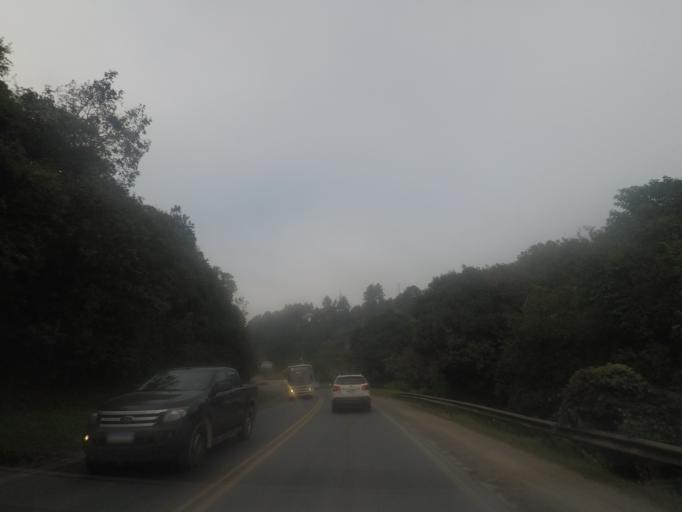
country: BR
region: Parana
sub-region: Almirante Tamandare
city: Almirante Tamandare
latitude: -25.3058
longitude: -49.3046
